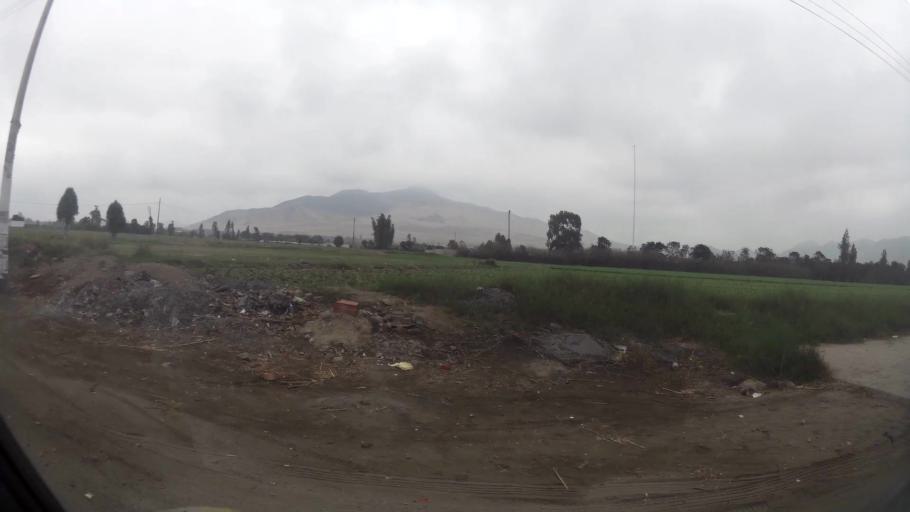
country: PE
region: Lima
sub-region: Provincia de Huaral
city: Huaral
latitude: -11.5236
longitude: -77.2458
